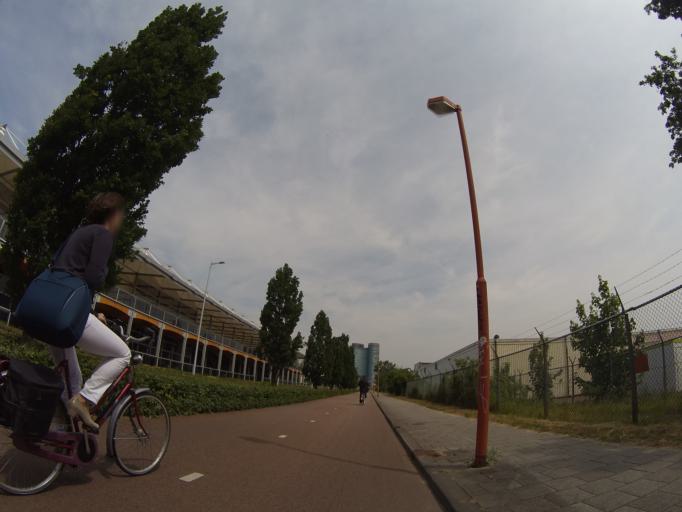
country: NL
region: Utrecht
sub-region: Gemeente Utrecht
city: Utrecht
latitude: 52.0800
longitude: 5.1033
